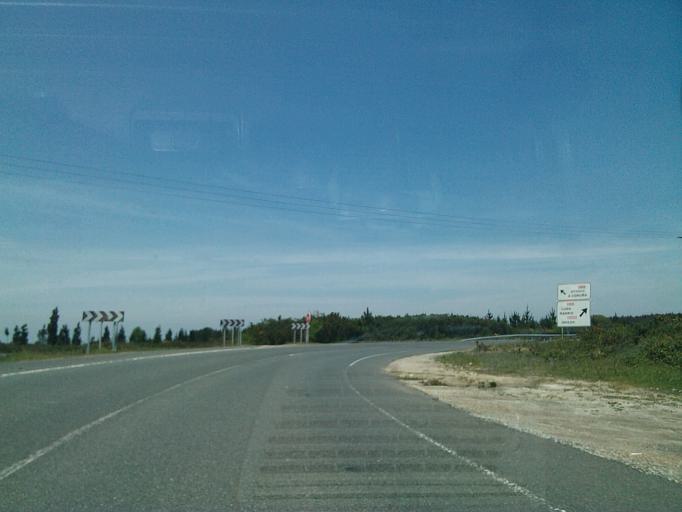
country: ES
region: Galicia
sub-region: Provincia de Lugo
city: Guitiriz
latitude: 43.1913
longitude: -7.9598
